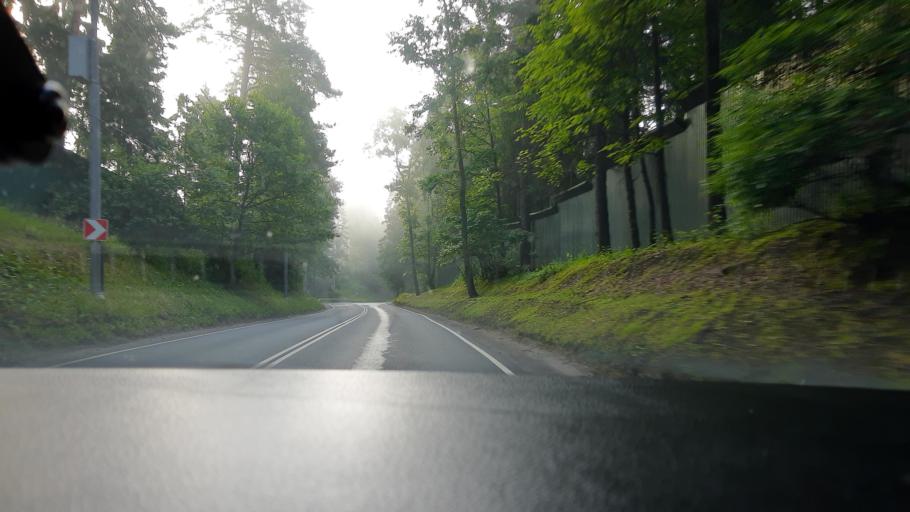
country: RU
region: Moskovskaya
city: Nikolina Gora
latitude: 55.7067
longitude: 37.0409
